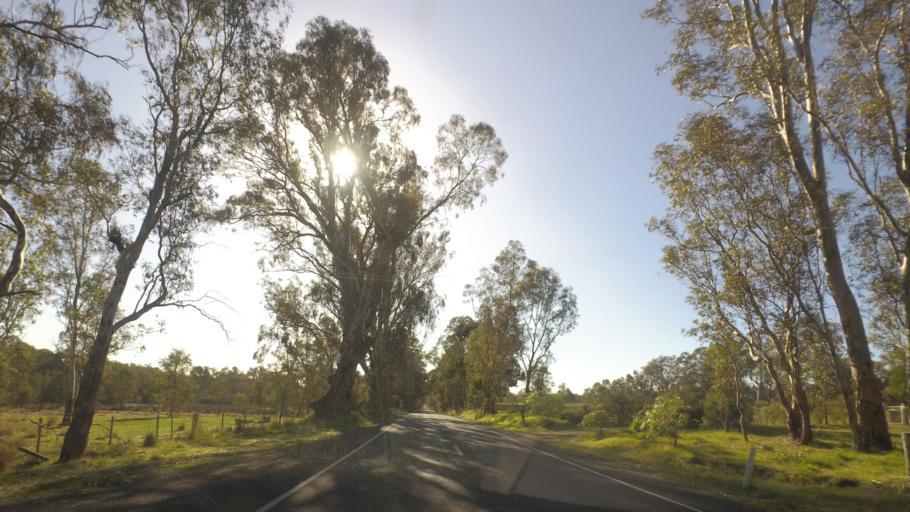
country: AU
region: Victoria
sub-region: Greater Bendigo
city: Kennington
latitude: -36.9337
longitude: 144.3440
